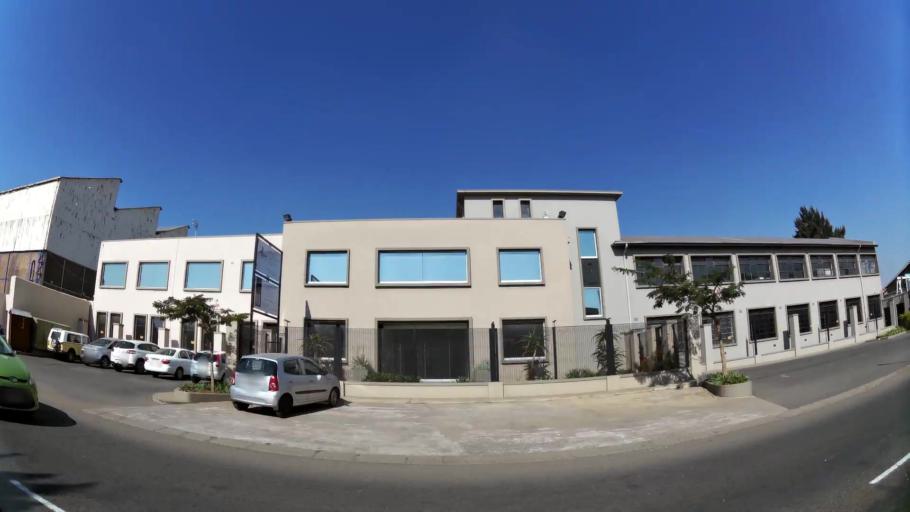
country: ZA
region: Gauteng
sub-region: Ekurhuleni Metropolitan Municipality
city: Benoni
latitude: -26.2071
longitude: 28.2964
